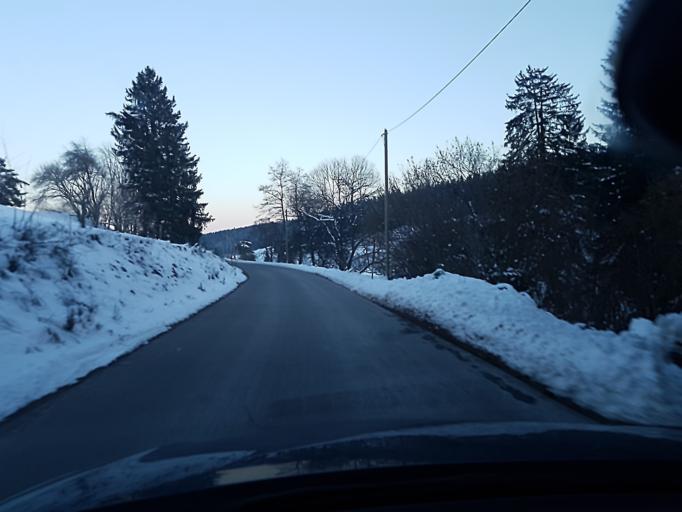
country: DE
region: Baden-Wuerttemberg
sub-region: Freiburg Region
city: Unterkirnach
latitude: 48.1095
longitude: 8.3625
